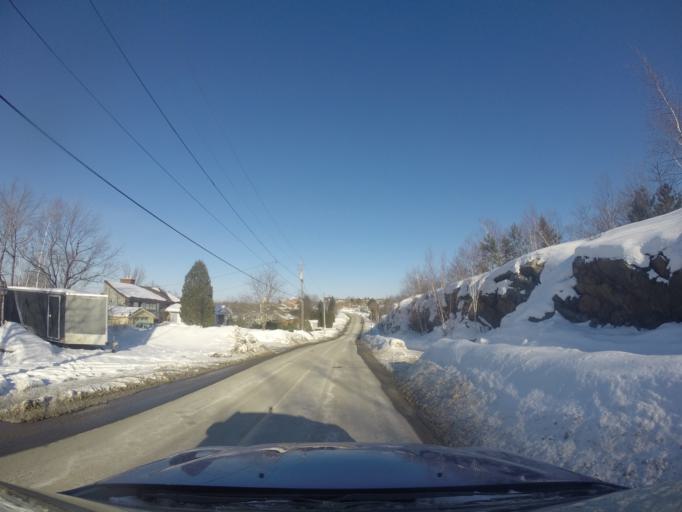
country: CA
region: Ontario
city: Greater Sudbury
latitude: 46.4571
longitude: -80.9942
